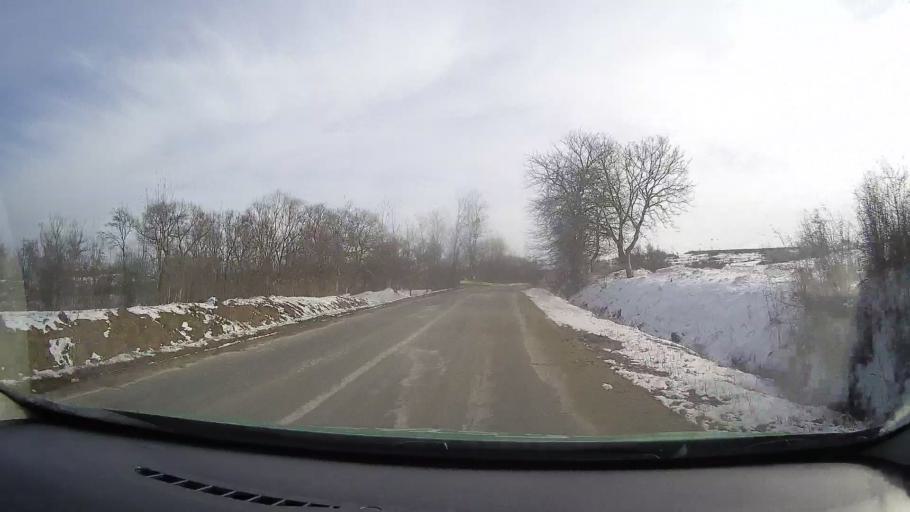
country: RO
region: Mures
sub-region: Comuna Apold
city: Apold
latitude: 46.1145
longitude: 24.8276
